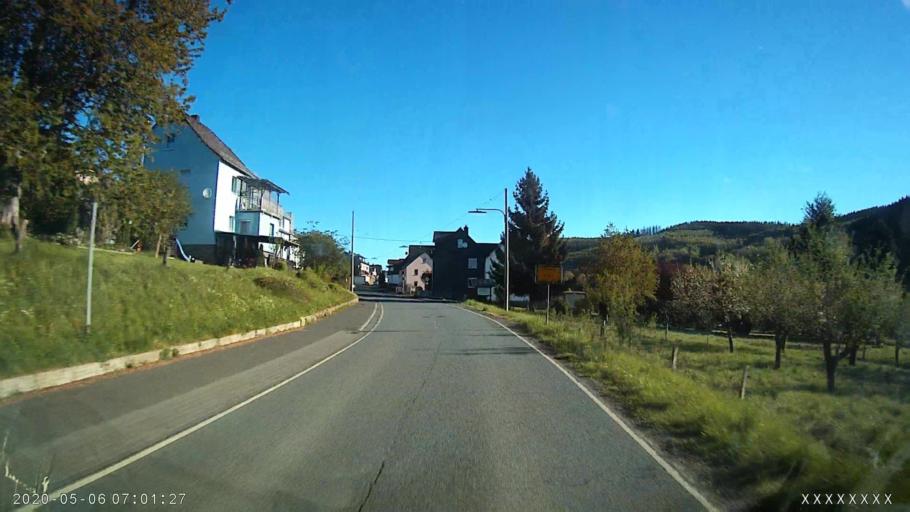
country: DE
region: Hesse
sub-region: Regierungsbezirk Giessen
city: Haiger
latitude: 50.7895
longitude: 8.2054
